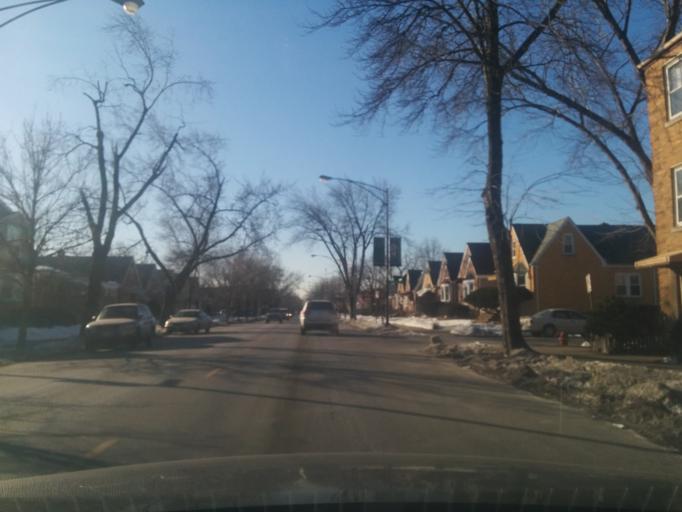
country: US
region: Illinois
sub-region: Cook County
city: Elmwood Park
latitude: 41.9378
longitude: -87.7762
